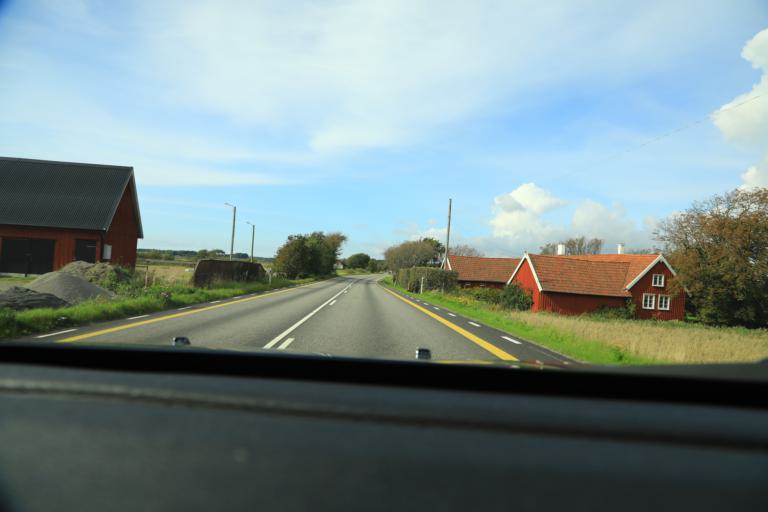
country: SE
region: Halland
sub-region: Varbergs Kommun
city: Traslovslage
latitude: 57.0319
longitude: 12.3303
